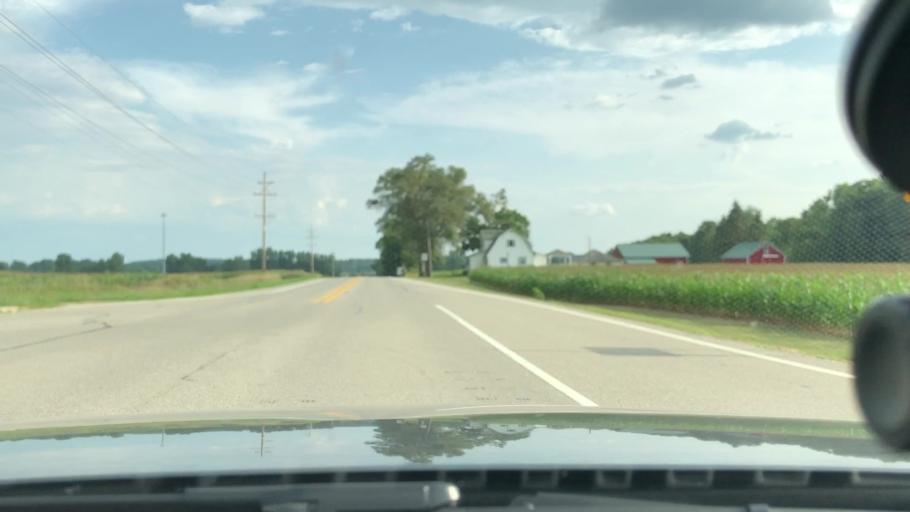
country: US
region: Michigan
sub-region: Washtenaw County
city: Chelsea
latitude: 42.2581
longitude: -84.0340
